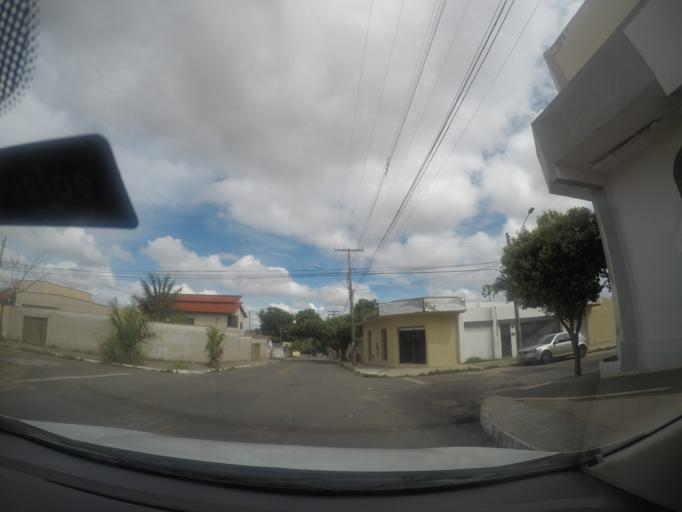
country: BR
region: Goias
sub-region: Goiania
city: Goiania
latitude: -16.6630
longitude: -49.2954
